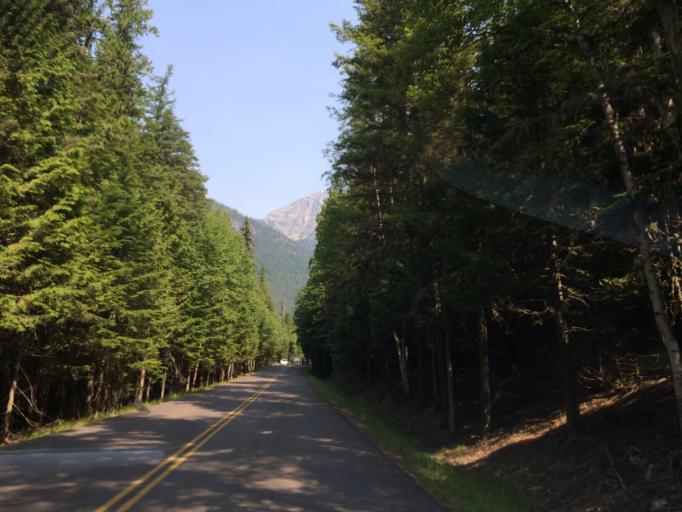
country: US
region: Montana
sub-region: Flathead County
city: Columbia Falls
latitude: 48.6363
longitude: -113.8638
